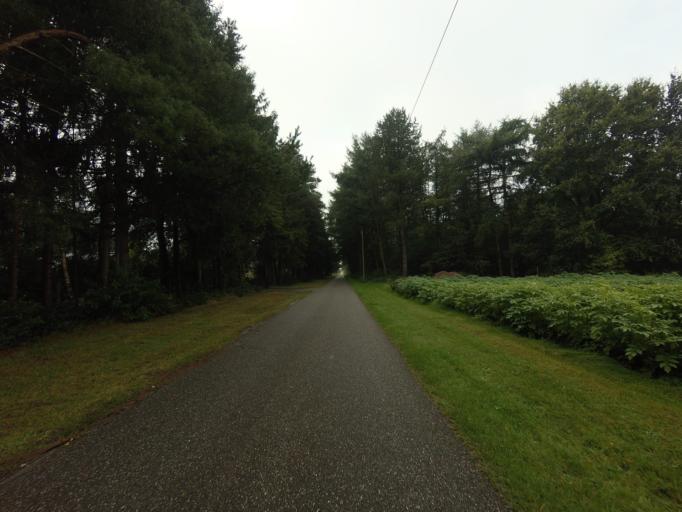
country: DE
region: Lower Saxony
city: Wielen
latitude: 52.5230
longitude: 6.7313
